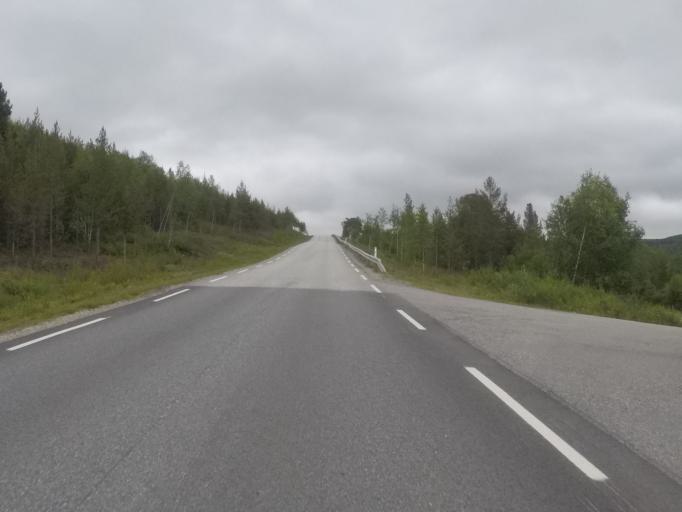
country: NO
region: Finnmark Fylke
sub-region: Karasjok
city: Karasjohka
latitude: 69.5732
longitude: 25.9149
